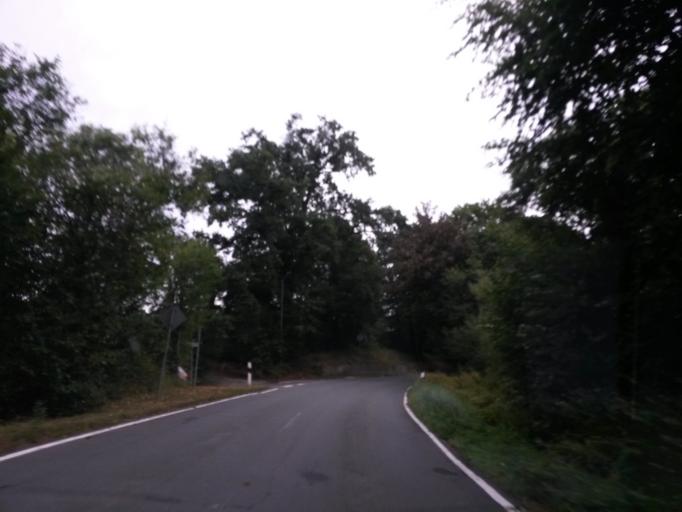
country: DE
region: North Rhine-Westphalia
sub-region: Regierungsbezirk Koln
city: Numbrecht
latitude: 50.8900
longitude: 7.5344
